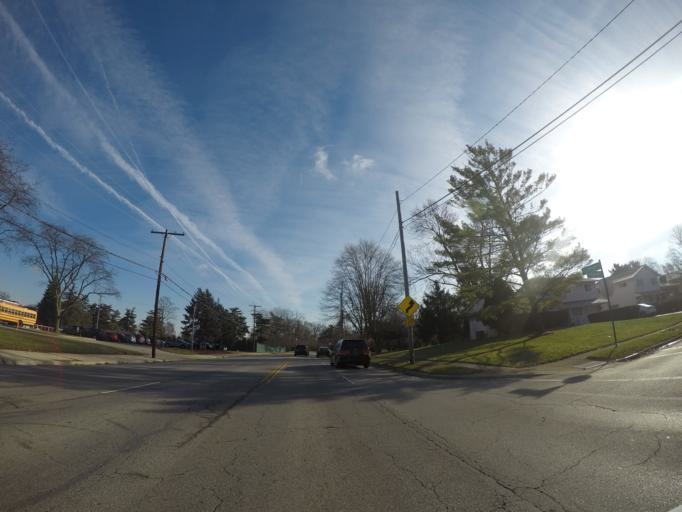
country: US
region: Ohio
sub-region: Franklin County
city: Upper Arlington
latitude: 40.0291
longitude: -83.0638
